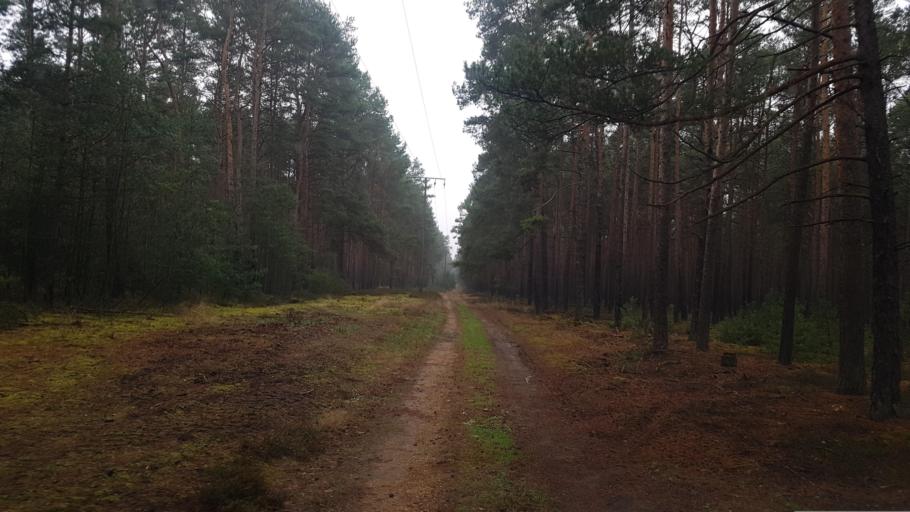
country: DE
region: Brandenburg
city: Sallgast
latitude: 51.6512
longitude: 13.7905
